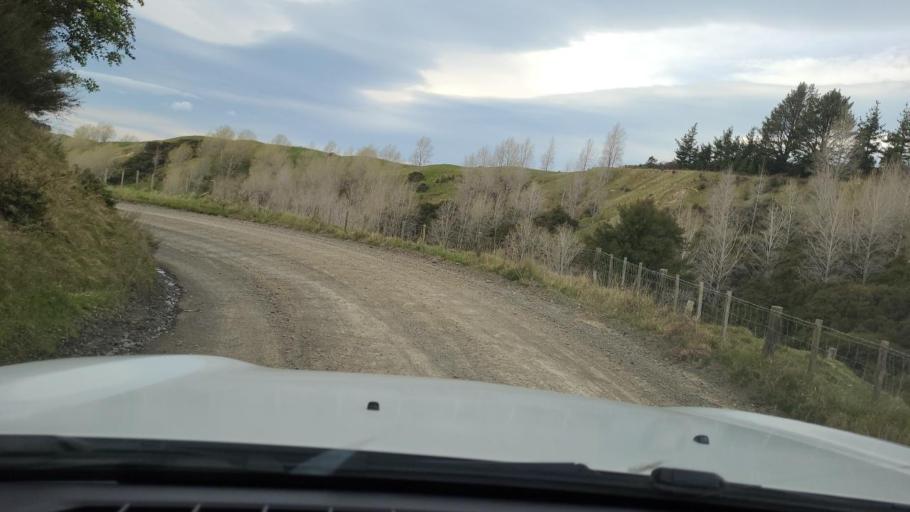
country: NZ
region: Hawke's Bay
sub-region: Napier City
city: Napier
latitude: -39.3059
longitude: 176.8230
